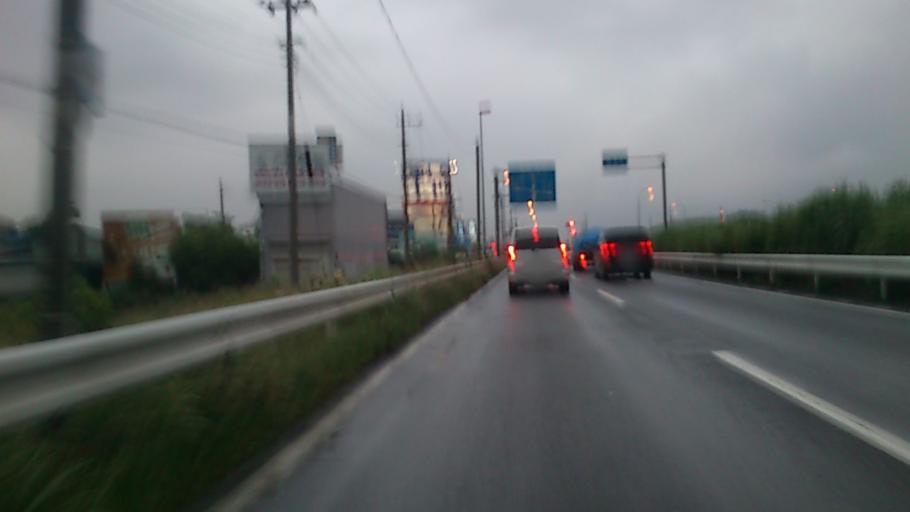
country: JP
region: Saitama
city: Kumagaya
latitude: 36.1530
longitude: 139.4166
